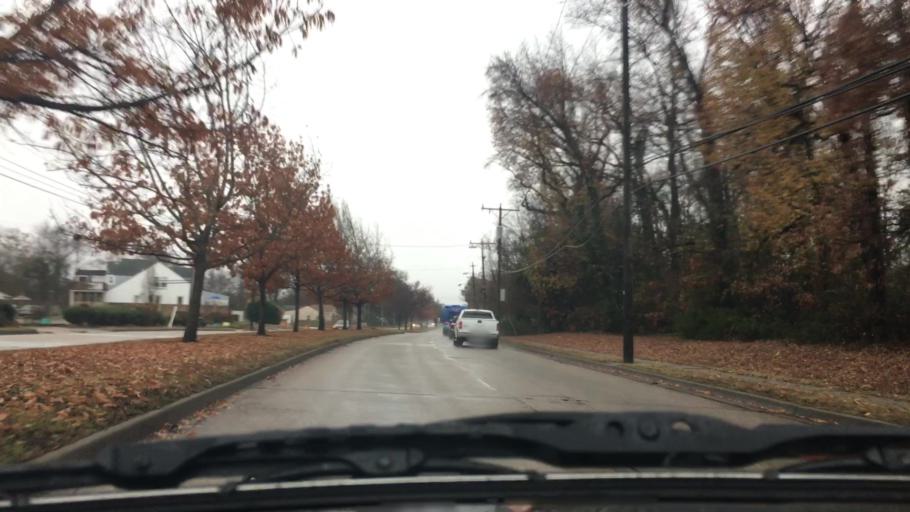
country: US
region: Virginia
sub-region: City of Norfolk
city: Norfolk
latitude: 36.9238
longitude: -76.2526
